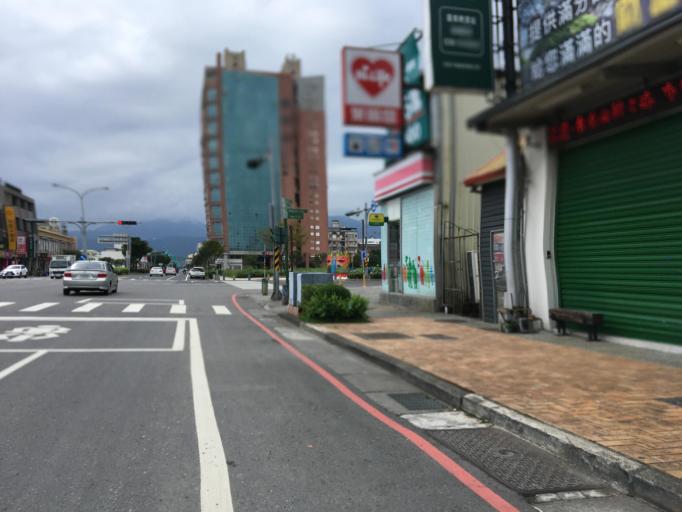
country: TW
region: Taiwan
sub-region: Yilan
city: Yilan
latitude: 24.6783
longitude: 121.7776
